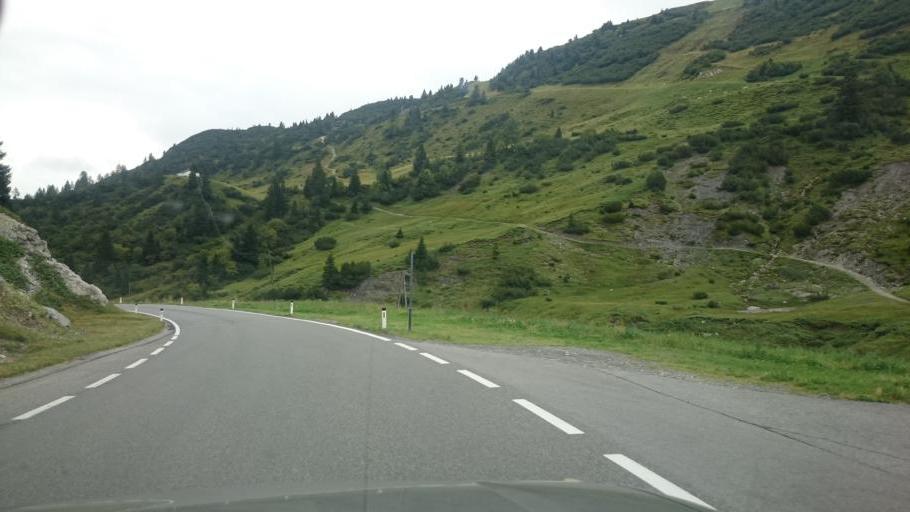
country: AT
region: Vorarlberg
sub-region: Politischer Bezirk Bregenz
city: Warth
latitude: 47.2676
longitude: 10.1501
